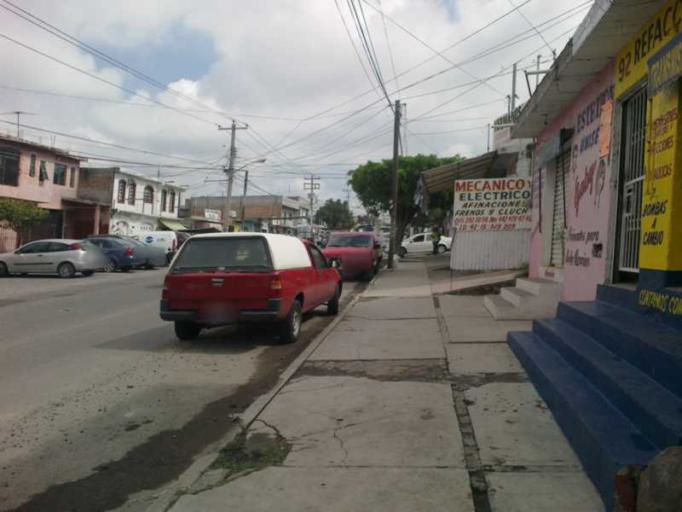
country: MX
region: Queretaro
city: San Jose el Alto
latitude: 20.6295
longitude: -100.3953
